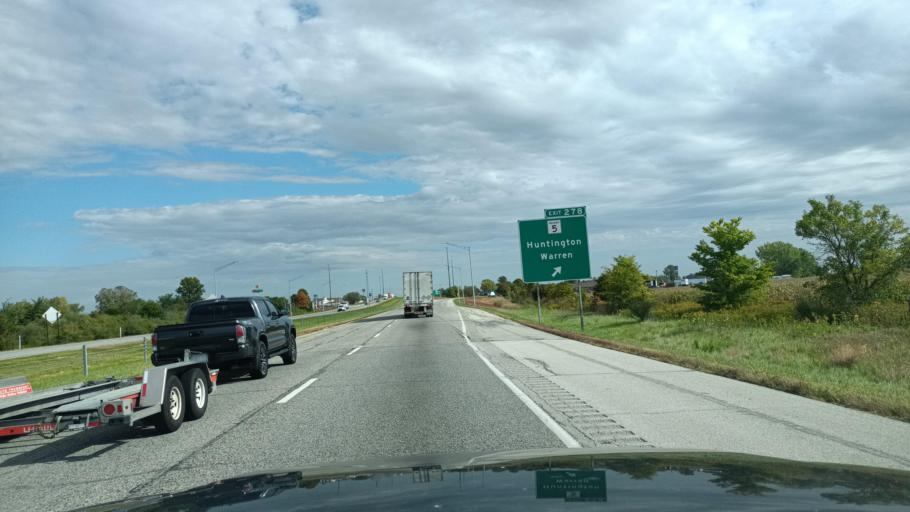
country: US
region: Indiana
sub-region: Huntington County
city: Warren
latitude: 40.7156
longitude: -85.4423
